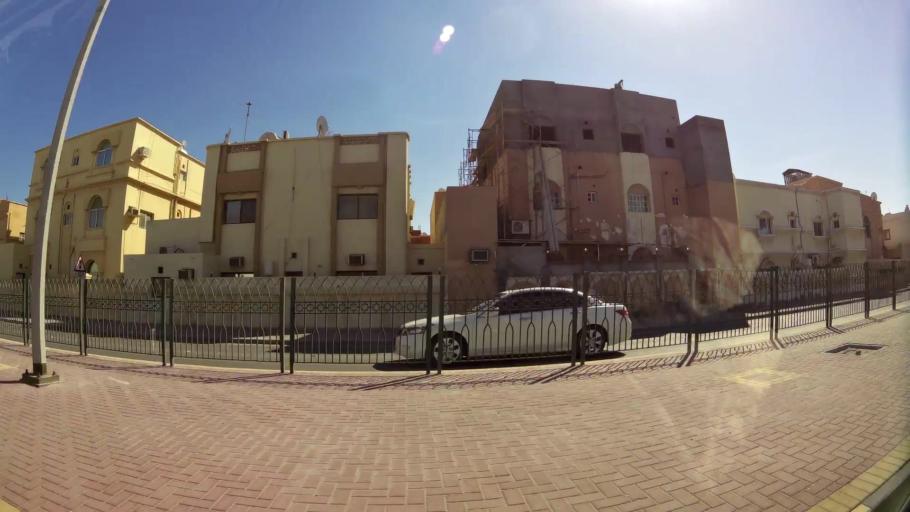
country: BH
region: Muharraq
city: Al Hadd
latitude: 26.2564
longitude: 50.6471
